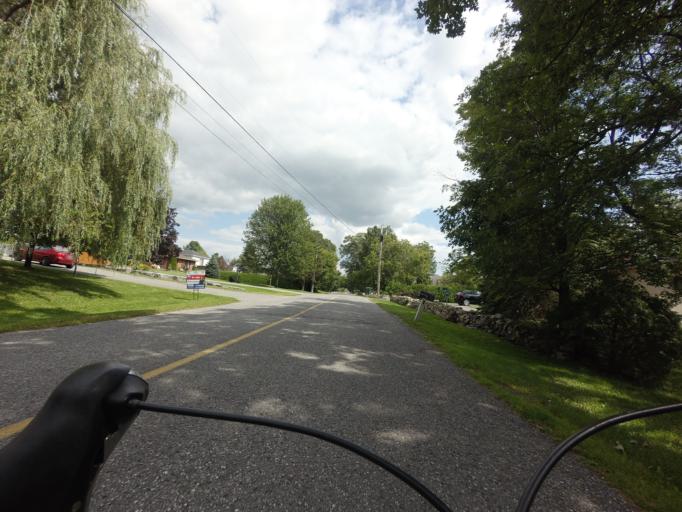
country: CA
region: Ontario
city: Bells Corners
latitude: 45.2652
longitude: -75.8222
